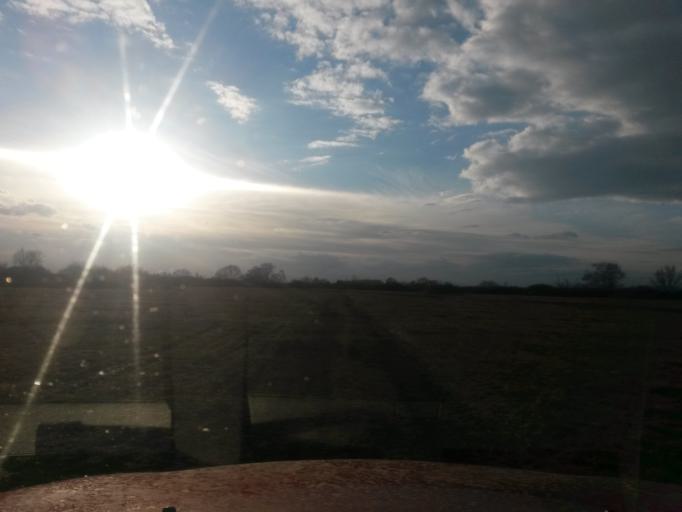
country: SK
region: Kosicky
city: Sobrance
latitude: 48.7032
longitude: 22.0778
